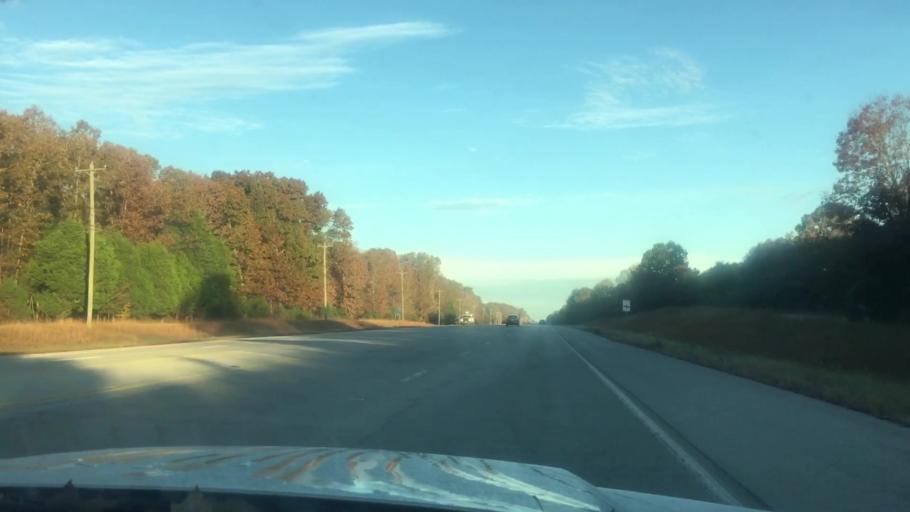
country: US
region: Tennessee
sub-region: Franklin County
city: Estill Springs
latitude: 35.3070
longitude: -86.1601
